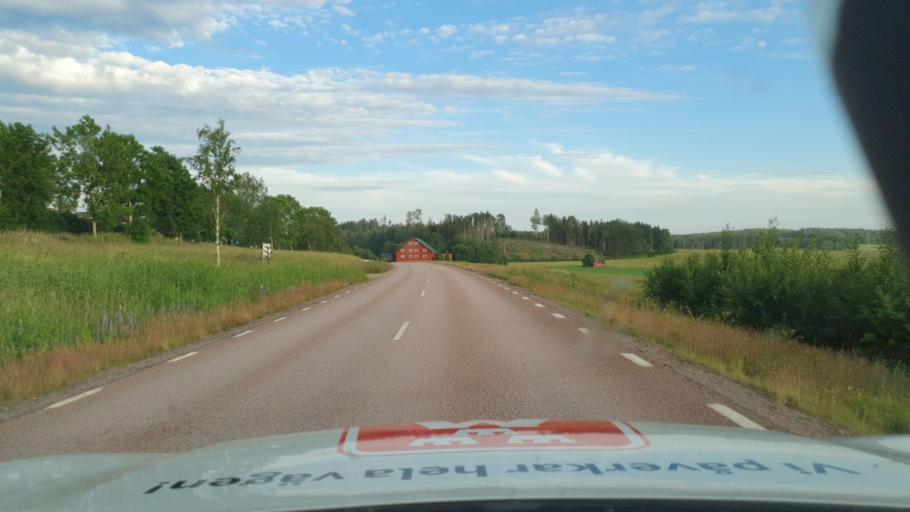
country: SE
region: Vaermland
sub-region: Karlstads Kommun
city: Molkom
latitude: 59.4714
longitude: 13.8094
